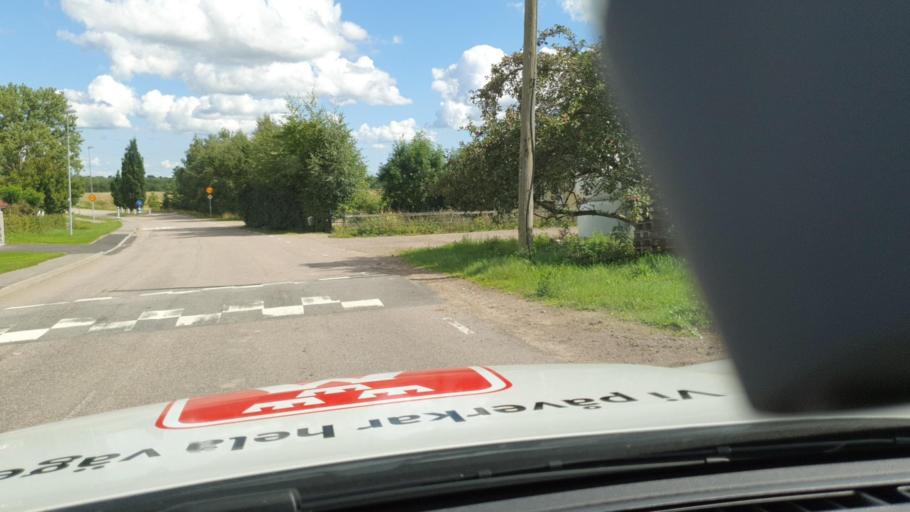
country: SE
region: Skane
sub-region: Astorps Kommun
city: Kvidinge
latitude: 56.1283
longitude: 13.0830
